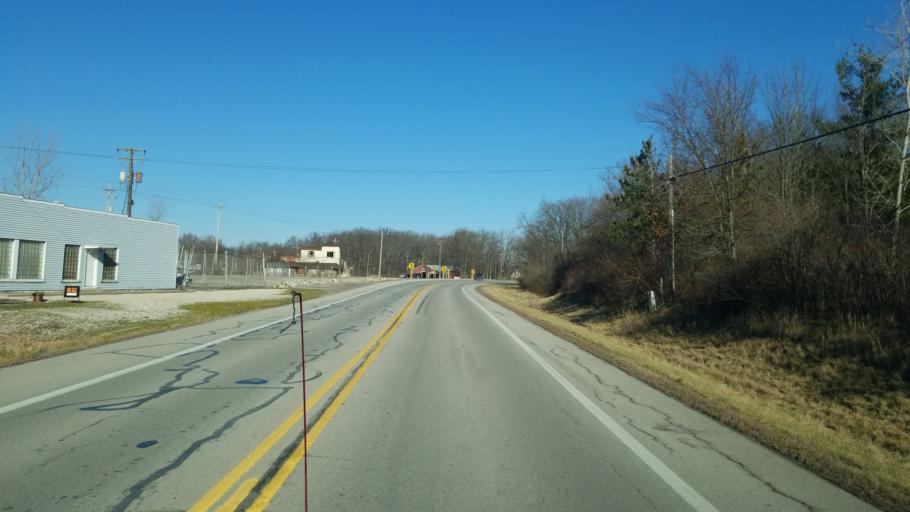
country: US
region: Ohio
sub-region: Wood County
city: Weston
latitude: 41.4221
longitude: -83.8546
